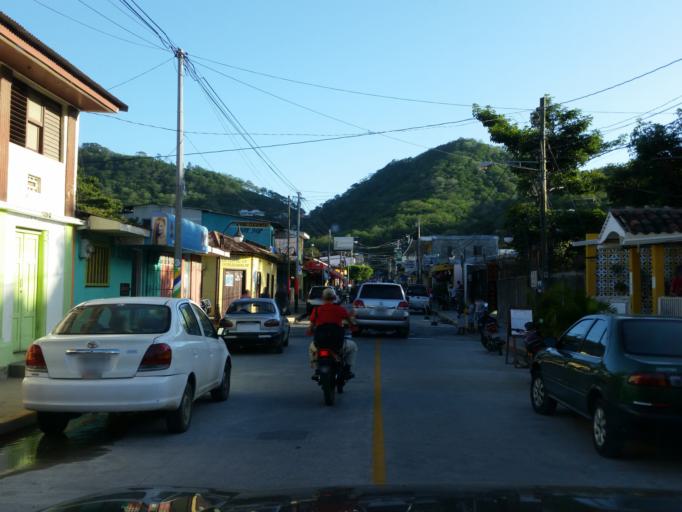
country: NI
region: Rivas
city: San Juan del Sur
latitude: 11.2544
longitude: -85.8708
